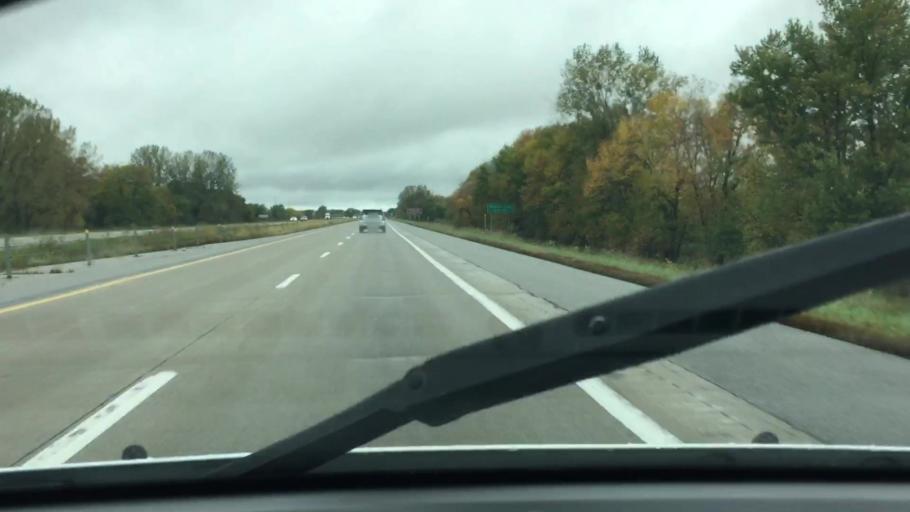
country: US
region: Iowa
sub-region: Jasper County
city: Colfax
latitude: 41.6961
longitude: -93.2284
